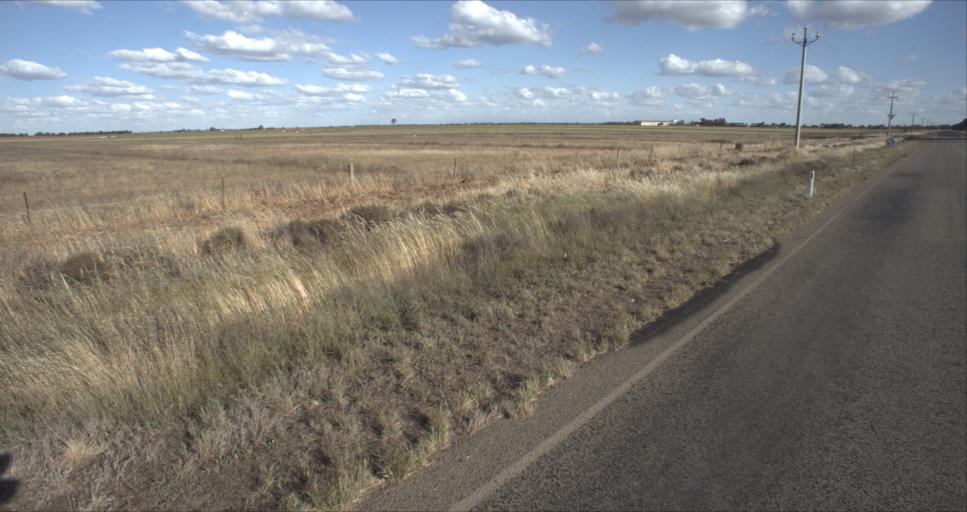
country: AU
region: New South Wales
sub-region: Leeton
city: Leeton
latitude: -34.5392
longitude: 146.2801
